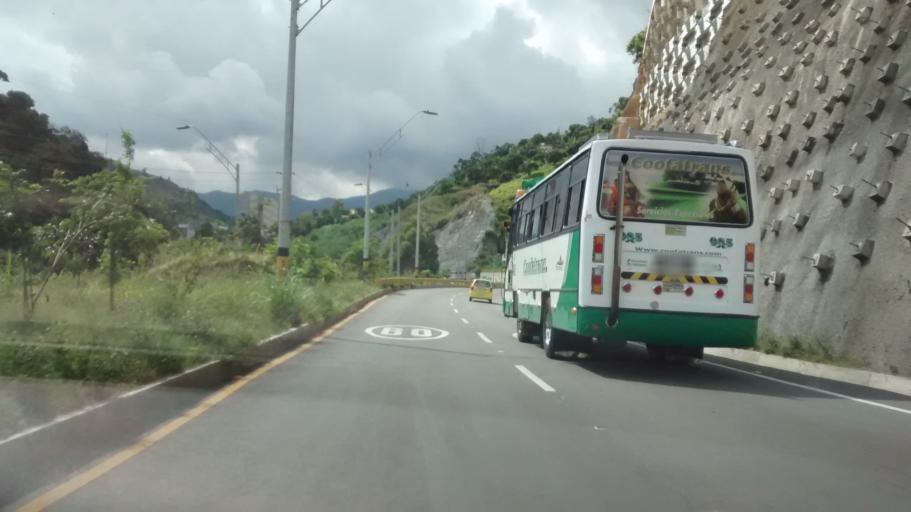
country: CO
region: Antioquia
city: Medellin
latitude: 6.2770
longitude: -75.6062
